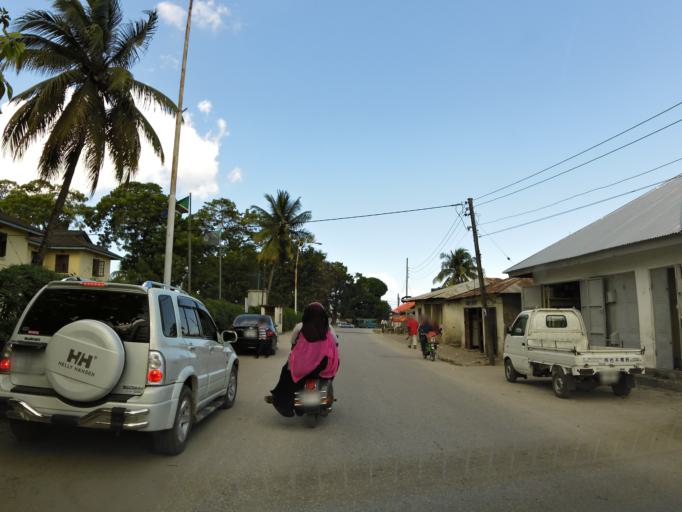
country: TZ
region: Zanzibar Urban/West
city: Zanzibar
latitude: -6.1634
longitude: 39.2077
